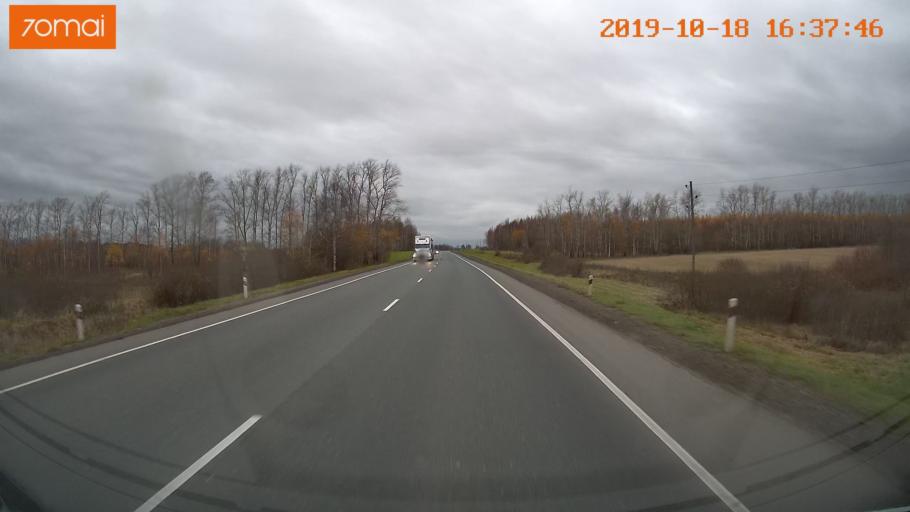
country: RU
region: Vladimir
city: Suzdal'
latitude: 56.4265
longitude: 40.4753
